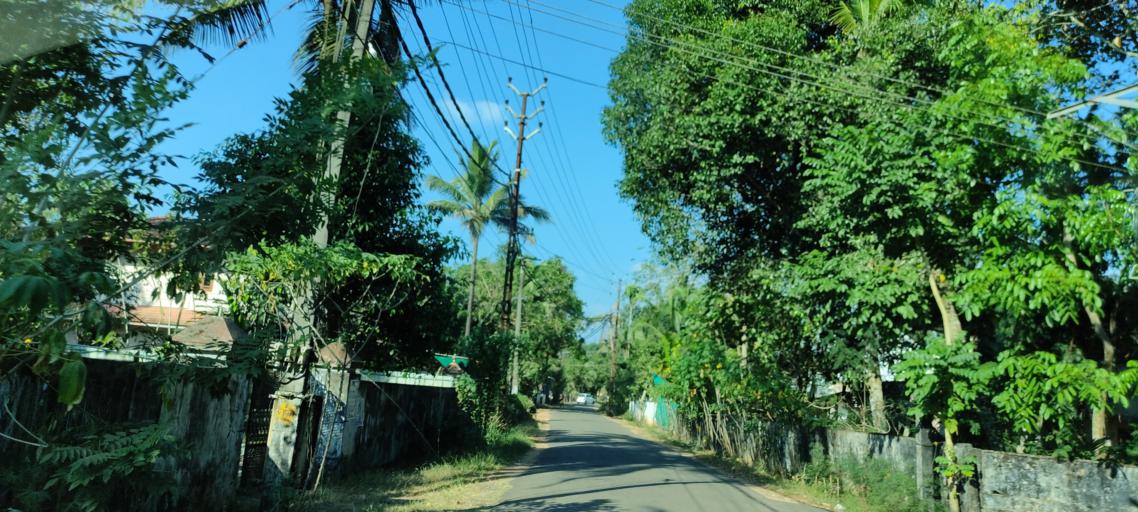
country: IN
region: Kerala
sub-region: Alappuzha
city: Shertallai
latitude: 9.6456
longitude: 76.3458
